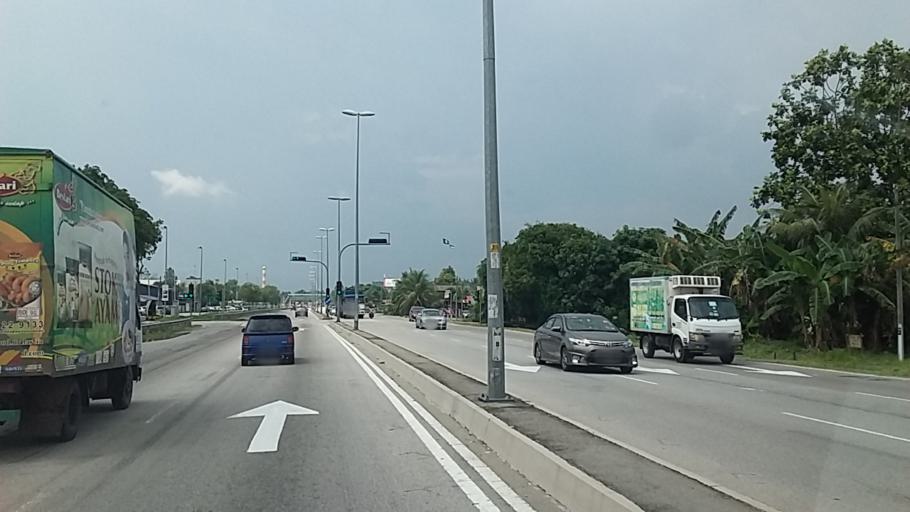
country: MY
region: Johor
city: Parit Raja
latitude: 1.8549
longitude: 103.0940
